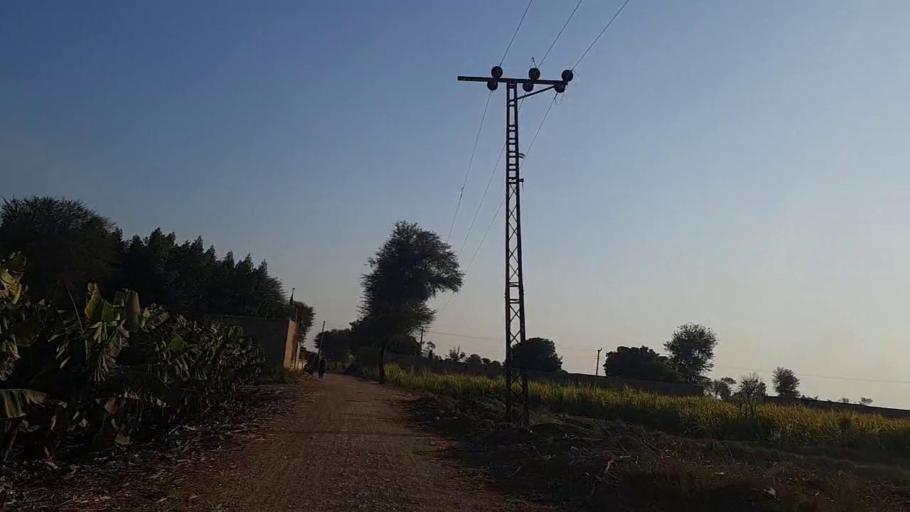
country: PK
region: Sindh
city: Sakrand
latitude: 26.3077
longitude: 68.1429
